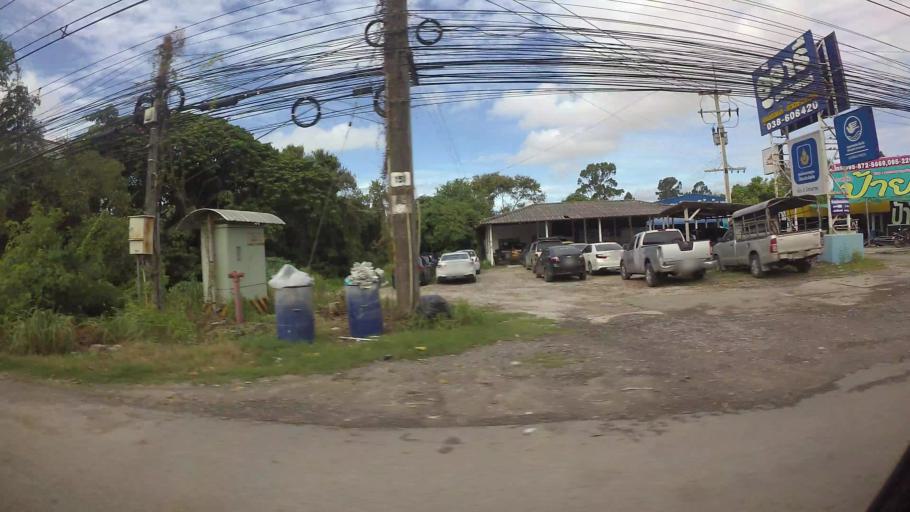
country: TH
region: Rayong
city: Rayong
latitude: 12.7097
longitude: 101.1744
